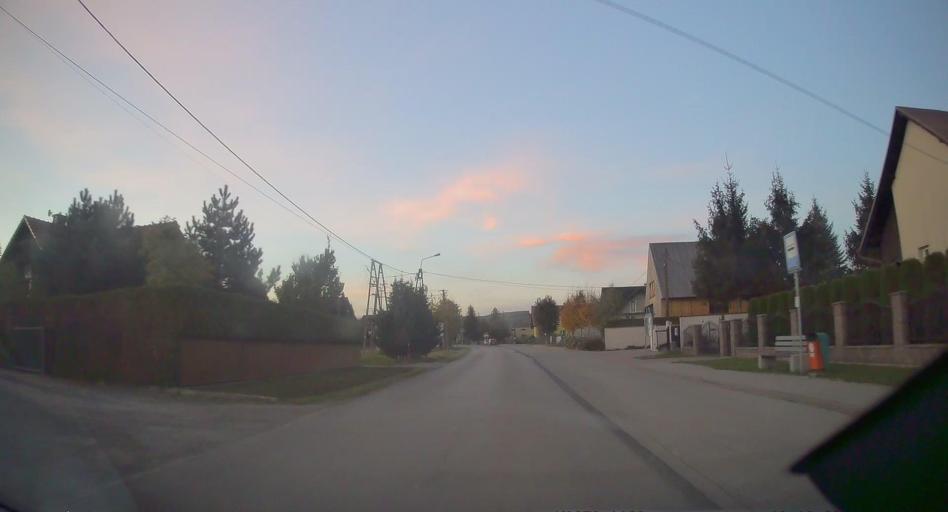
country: PL
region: Lesser Poland Voivodeship
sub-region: Powiat krakowski
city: Zabierzow
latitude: 50.1323
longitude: 19.8216
